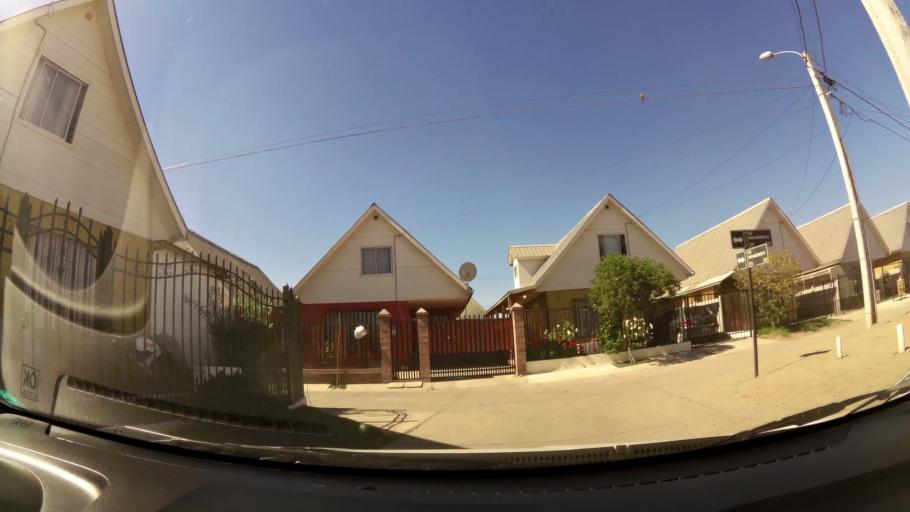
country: CL
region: O'Higgins
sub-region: Provincia de Cachapoal
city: Rancagua
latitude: -34.1773
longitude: -70.7770
